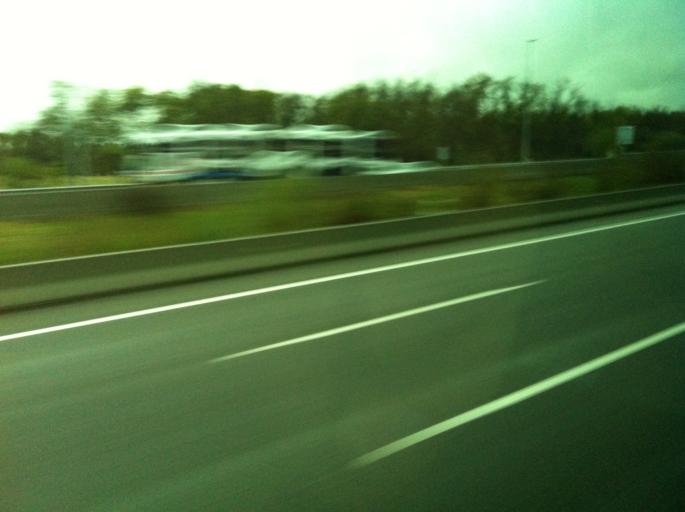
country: ES
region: Madrid
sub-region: Provincia de Madrid
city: Alpedrete
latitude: 40.6466
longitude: -4.0512
